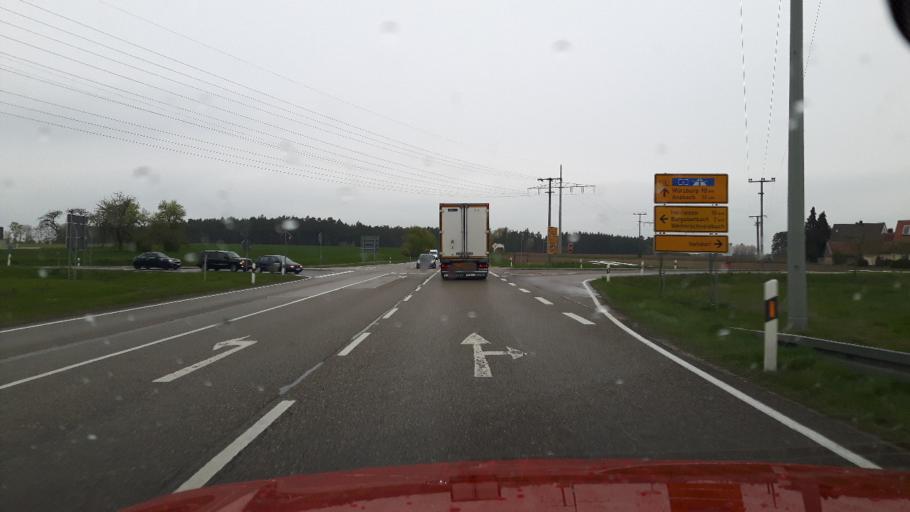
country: DE
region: Bavaria
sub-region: Regierungsbezirk Mittelfranken
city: Weidenbach
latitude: 49.2302
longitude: 10.6224
